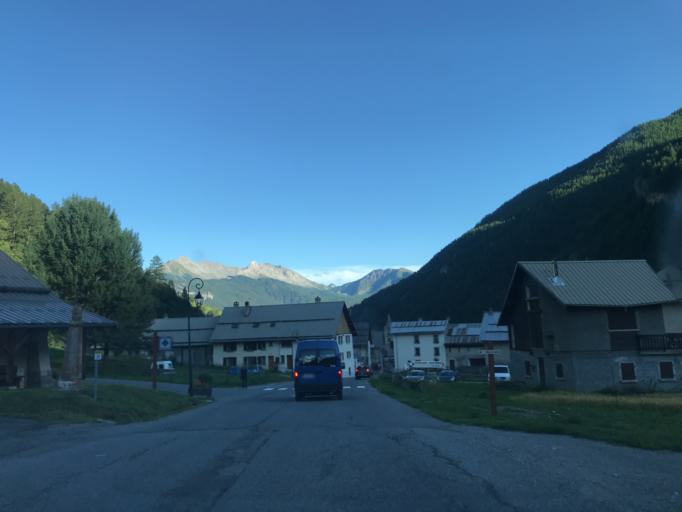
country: FR
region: Provence-Alpes-Cote d'Azur
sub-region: Departement des Hautes-Alpes
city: Guillestre
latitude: 44.7689
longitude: 6.7374
